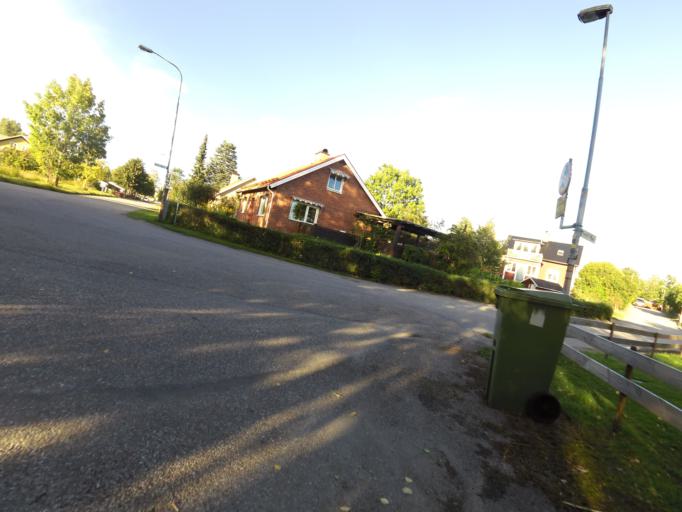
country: SE
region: Gaevleborg
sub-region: Gavle Kommun
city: Gavle
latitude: 60.7231
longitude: 17.1666
